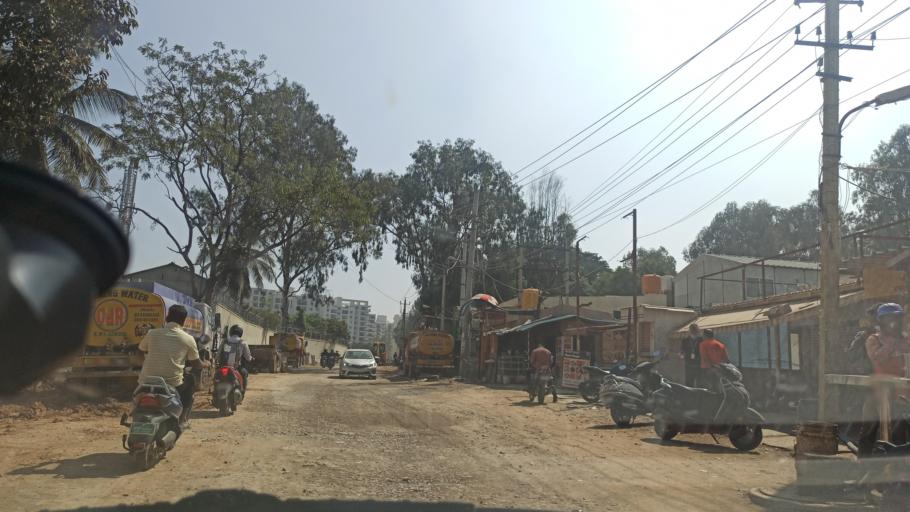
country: IN
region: Karnataka
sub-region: Bangalore Urban
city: Bangalore
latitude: 12.9188
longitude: 77.6855
